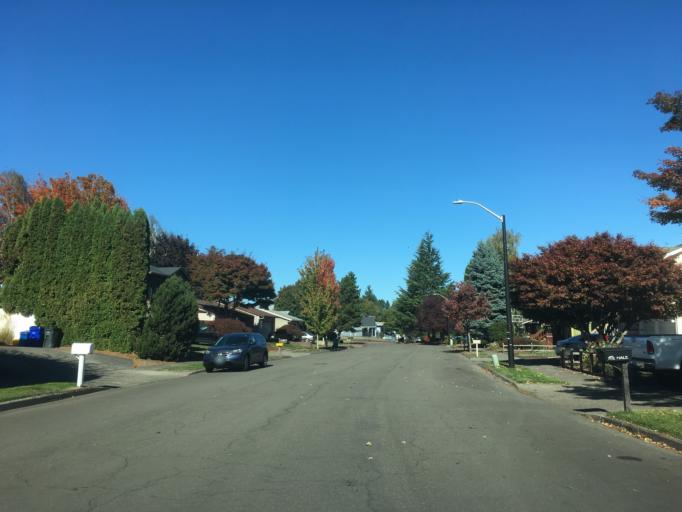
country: US
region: Oregon
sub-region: Multnomah County
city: Gresham
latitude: 45.4828
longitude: -122.4015
